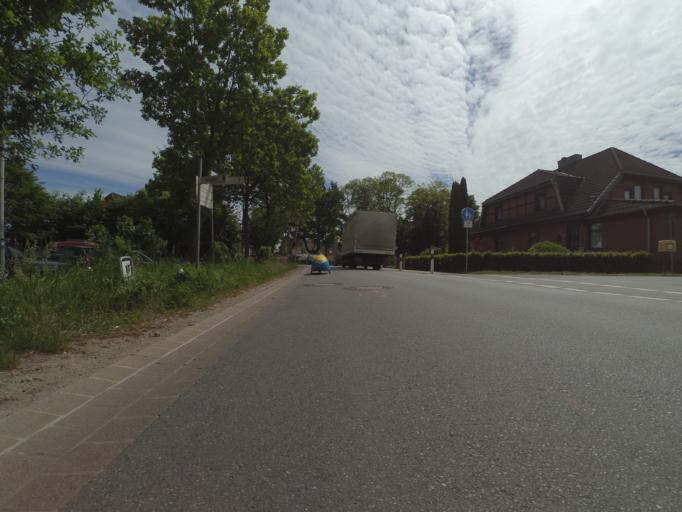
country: DE
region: Lower Saxony
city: Neustadt am Rubenberge
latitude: 52.4673
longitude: 9.4535
